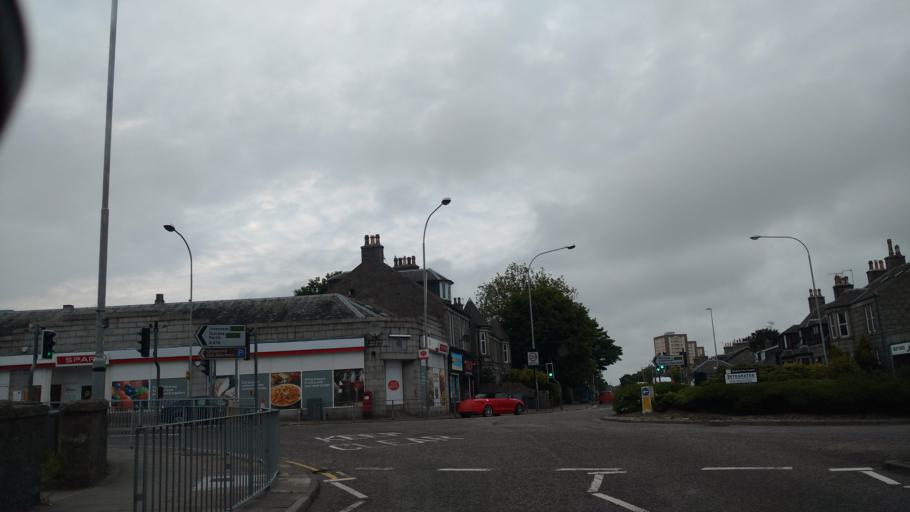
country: GB
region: Scotland
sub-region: Aberdeen City
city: Aberdeen
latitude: 57.1666
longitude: -2.0972
